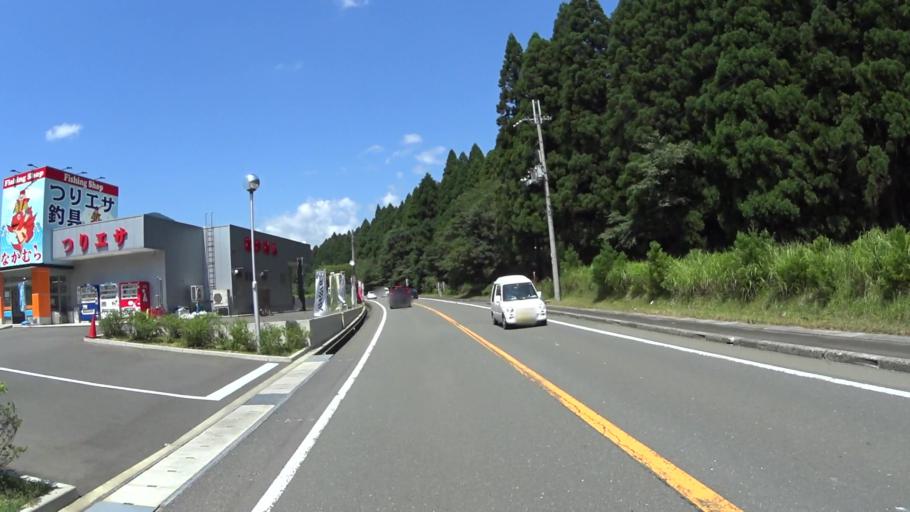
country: JP
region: Fukui
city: Obama
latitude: 35.4167
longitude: 135.9494
